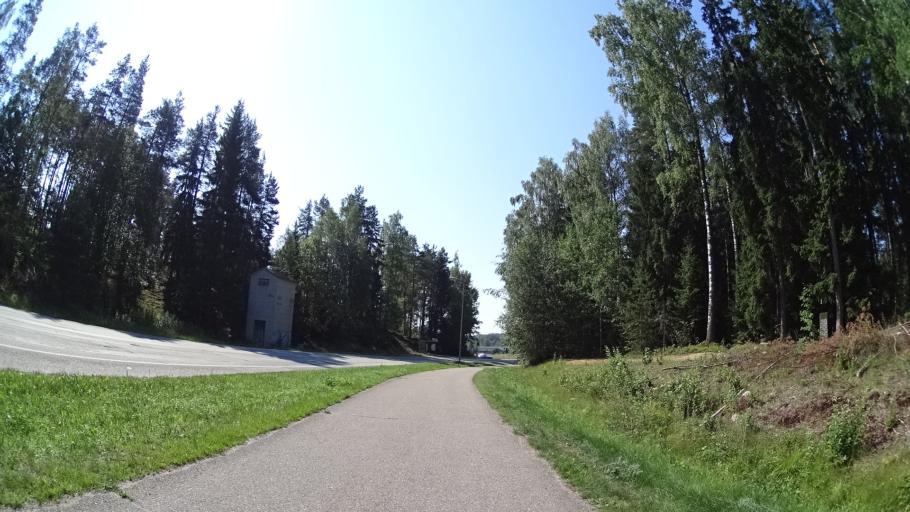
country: FI
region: Uusimaa
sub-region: Helsinki
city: Kerava
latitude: 60.3694
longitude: 25.0754
